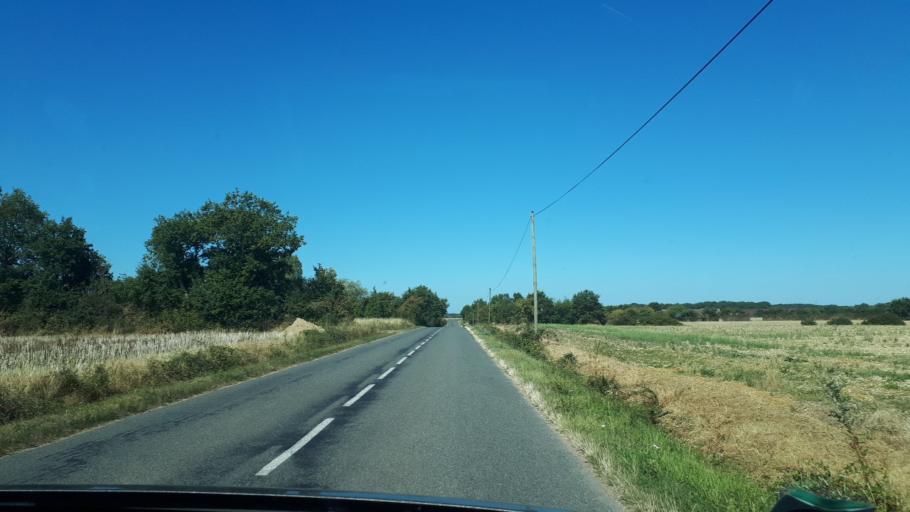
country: FR
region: Centre
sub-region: Departement du Loiret
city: Autry-le-Chatel
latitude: 47.6070
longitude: 2.5748
